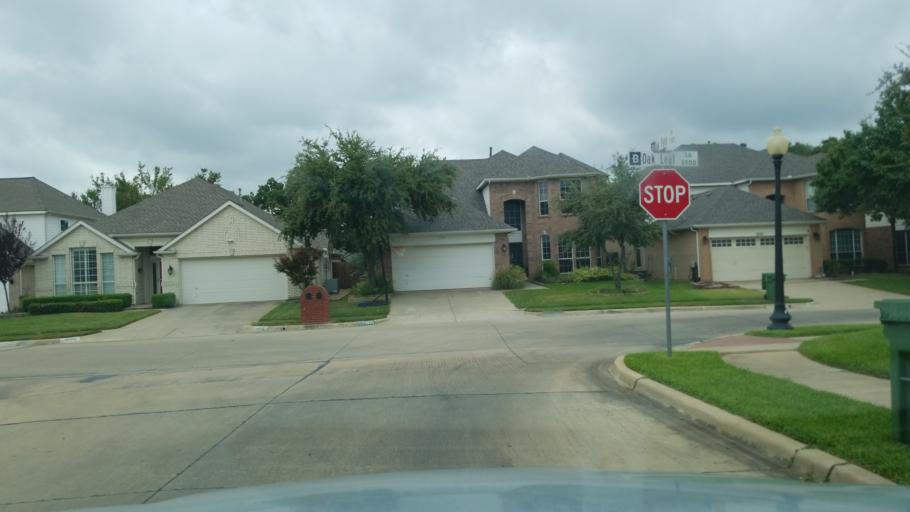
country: US
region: Texas
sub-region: Tarrant County
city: Euless
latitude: 32.8435
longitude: -97.1046
